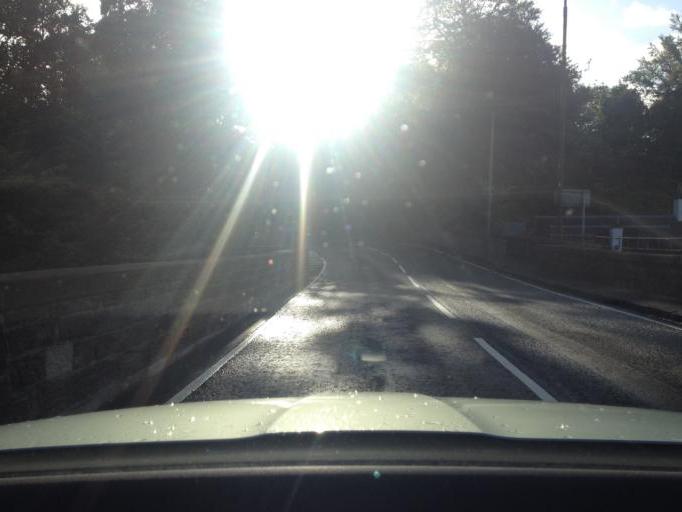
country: GB
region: Scotland
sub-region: West Lothian
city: Mid Calder
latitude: 55.8927
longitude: -3.4779
